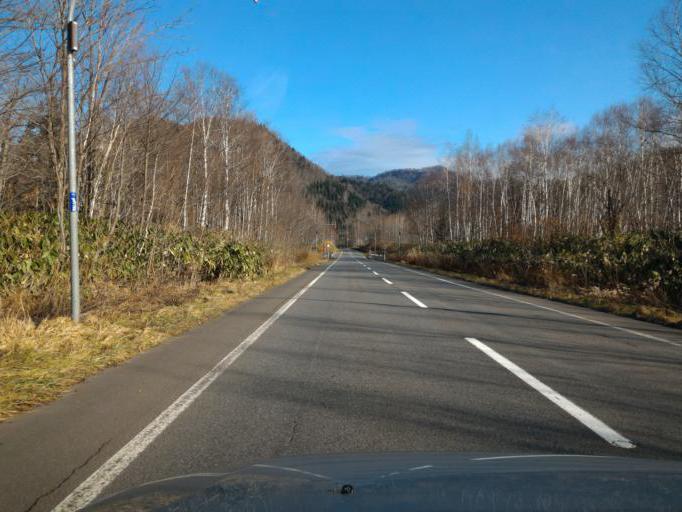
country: JP
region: Hokkaido
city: Ashibetsu
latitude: 43.3242
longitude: 142.1509
